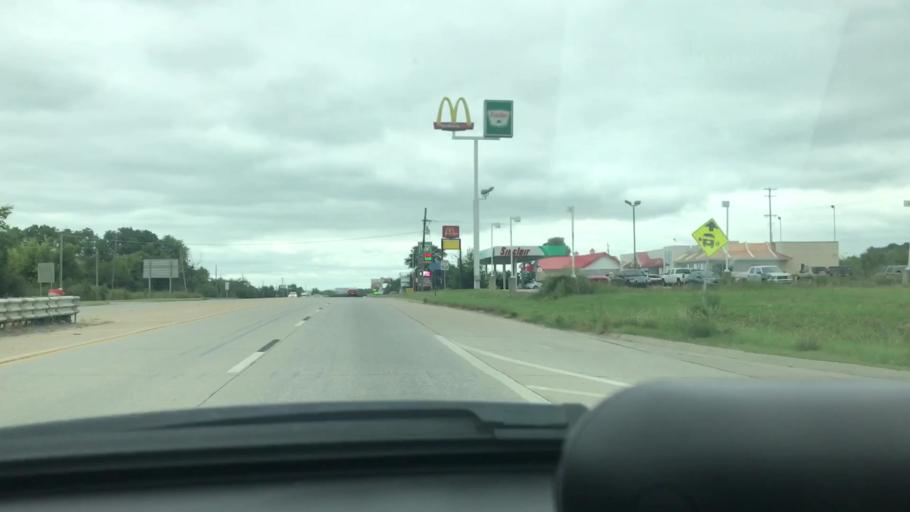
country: US
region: Oklahoma
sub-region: Mayes County
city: Chouteau
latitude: 36.1684
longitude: -95.3418
